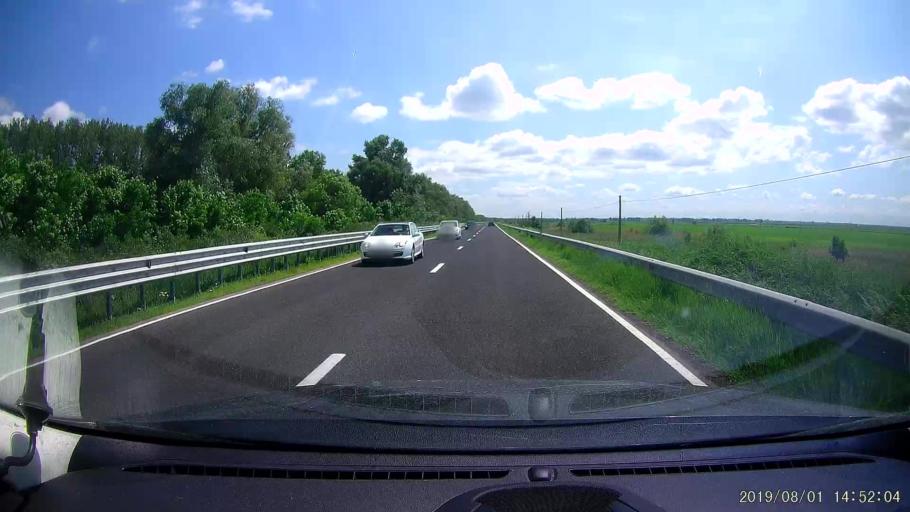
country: RO
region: Braila
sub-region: Comuna Vadeni
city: Vadeni
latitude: 45.3632
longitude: 28.0133
